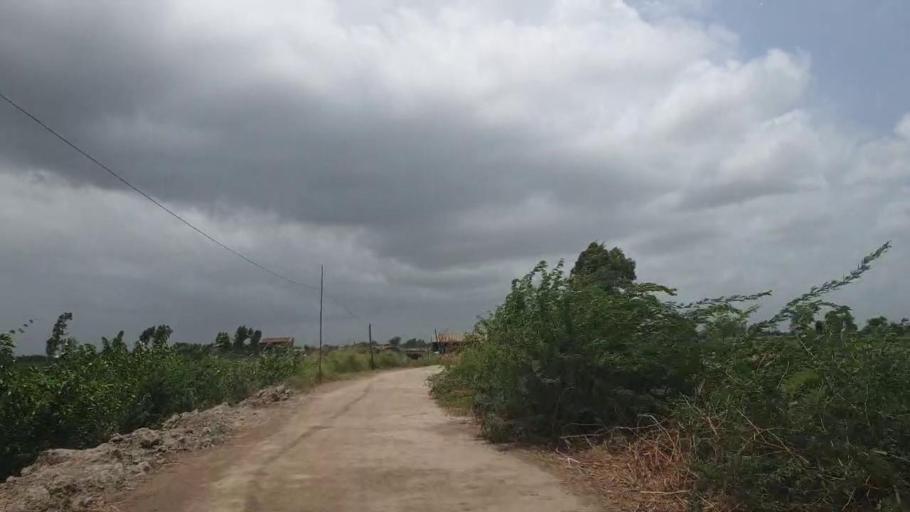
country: PK
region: Sindh
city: Badin
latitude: 24.6634
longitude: 68.9063
